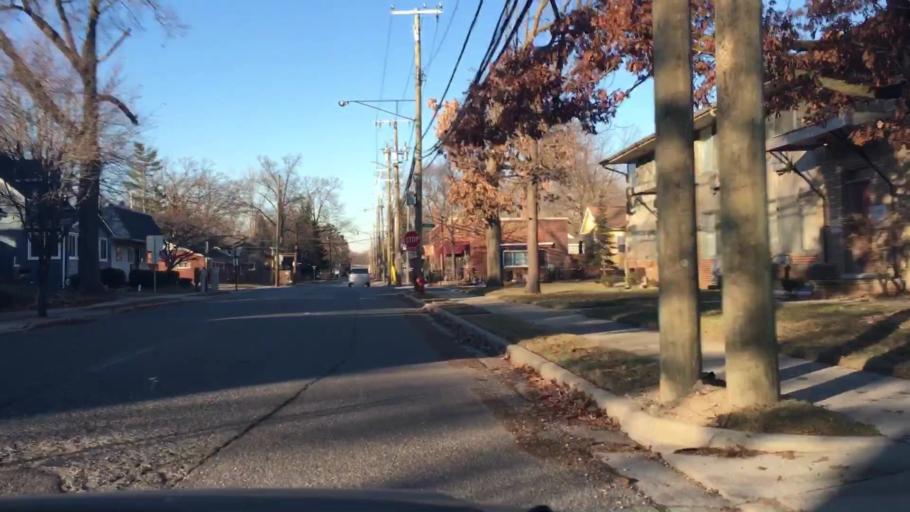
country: US
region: Michigan
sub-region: Oakland County
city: Ferndale
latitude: 42.4543
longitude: -83.1378
